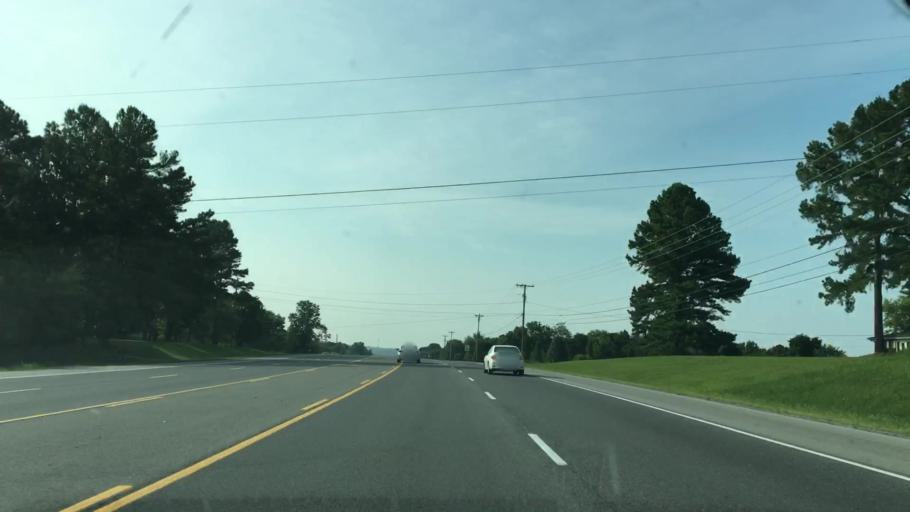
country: US
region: Tennessee
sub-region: Wilson County
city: Mount Juliet
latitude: 36.2079
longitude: -86.4196
